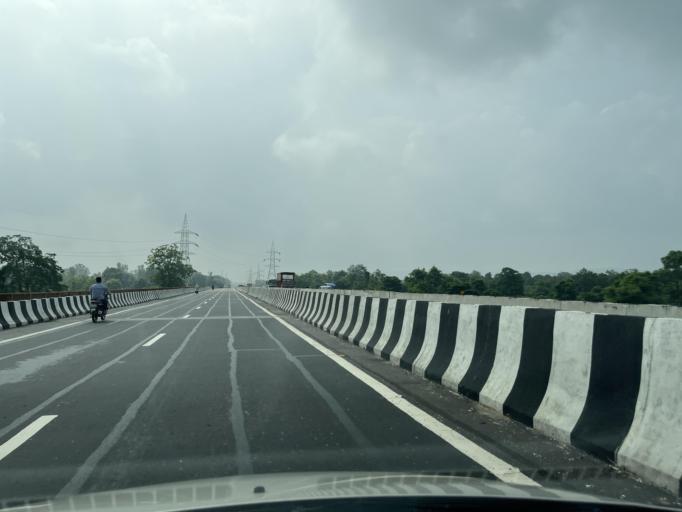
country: IN
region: Uttarakhand
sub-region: Dehradun
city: Raiwala
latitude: 30.0995
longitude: 78.1786
